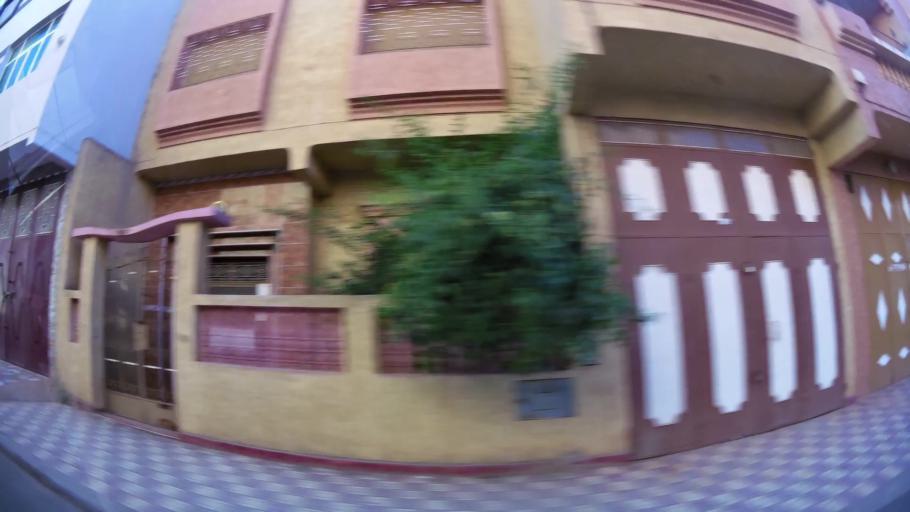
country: MA
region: Oriental
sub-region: Berkane-Taourirt
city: Berkane
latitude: 34.9304
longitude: -2.3410
